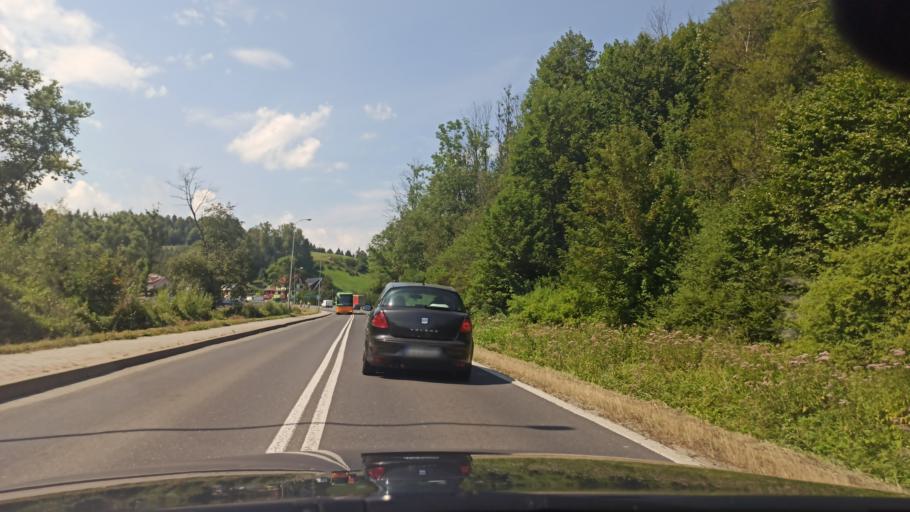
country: PL
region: Lesser Poland Voivodeship
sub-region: Powiat nowotarski
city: Kroscienko nad Dunajcem
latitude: 49.4392
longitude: 20.4014
